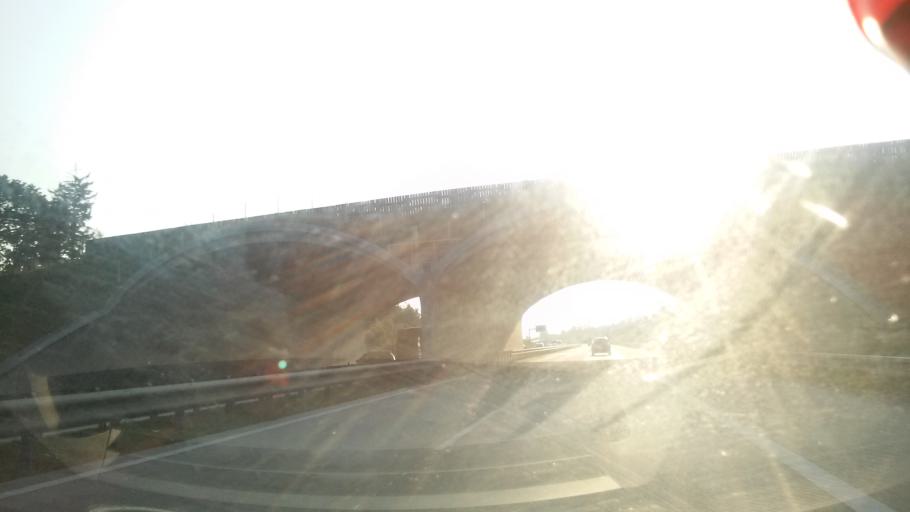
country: CZ
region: Central Bohemia
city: Jesenice
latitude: 49.9626
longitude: 14.5354
